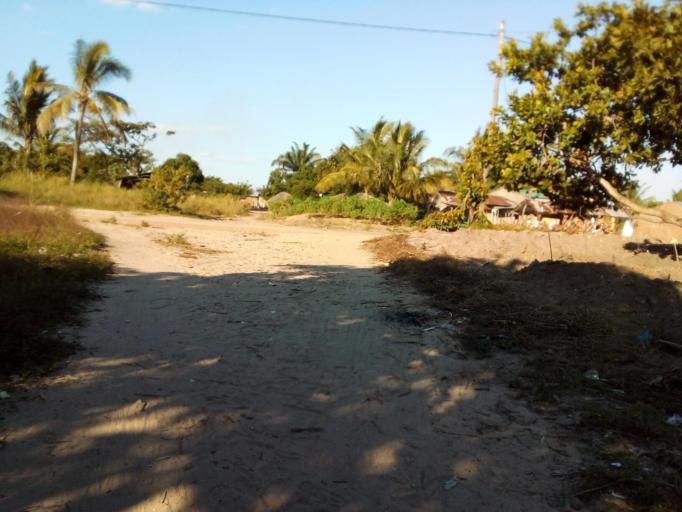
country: MZ
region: Zambezia
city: Quelimane
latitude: -17.5588
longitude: 36.6985
